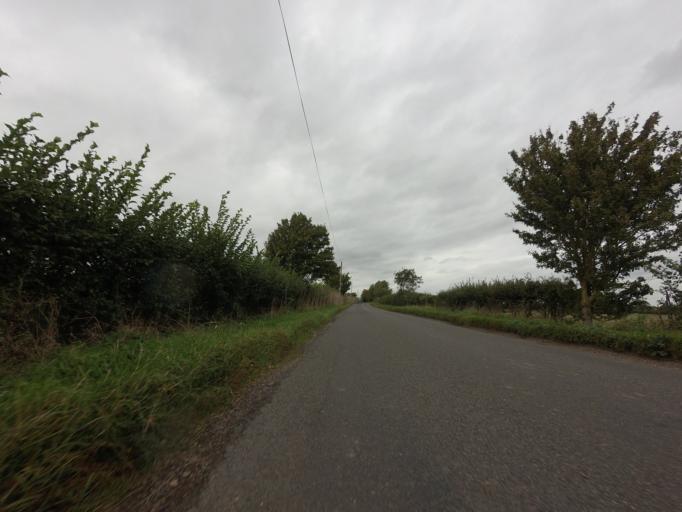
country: GB
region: England
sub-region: Cambridgeshire
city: Harston
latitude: 52.1021
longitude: 0.0563
